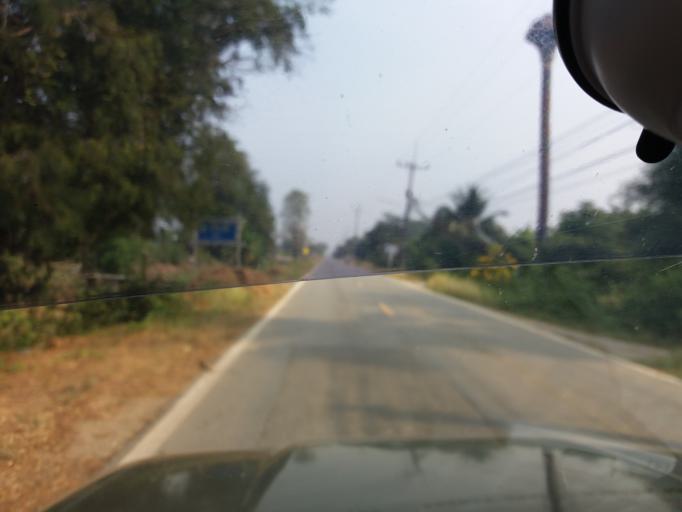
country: TH
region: Suphan Buri
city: Doem Bang Nang Buat
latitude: 14.8767
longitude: 100.1762
